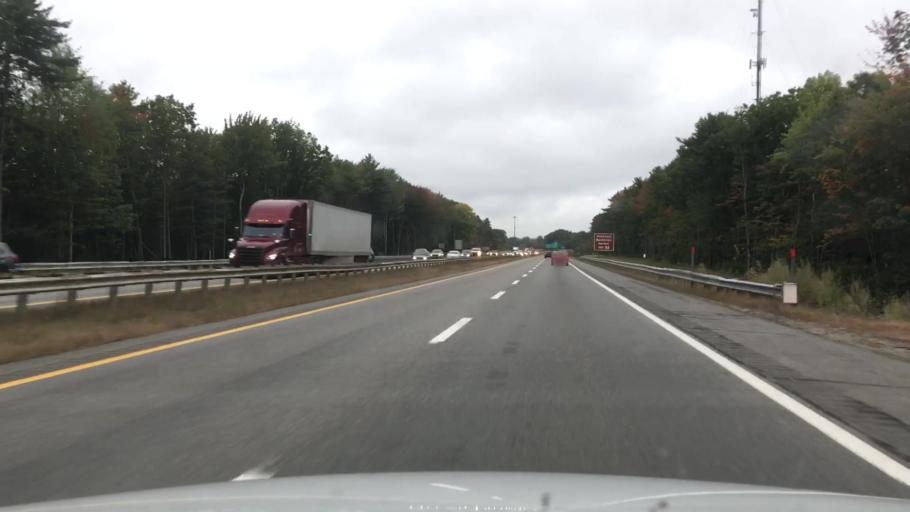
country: US
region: Maine
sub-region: Cumberland County
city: Westbrook
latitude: 43.7042
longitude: -70.3128
